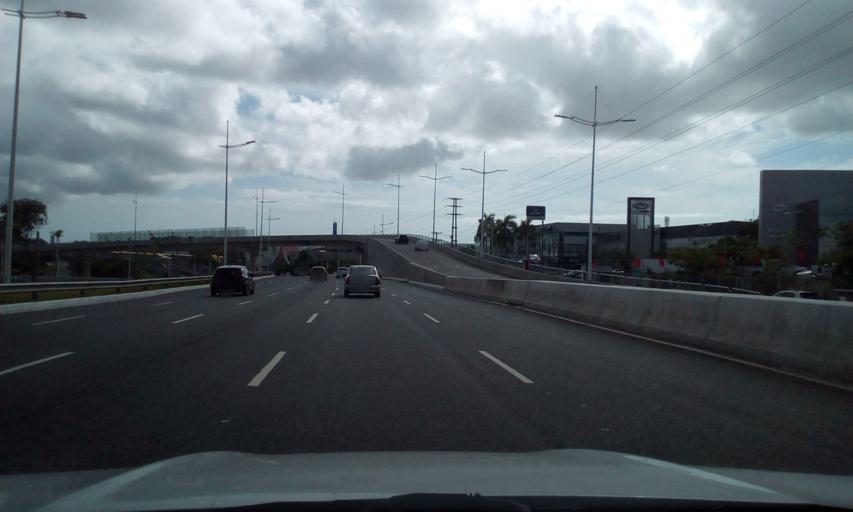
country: BR
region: Bahia
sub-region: Lauro De Freitas
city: Lauro de Freitas
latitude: -12.9375
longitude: -38.4000
